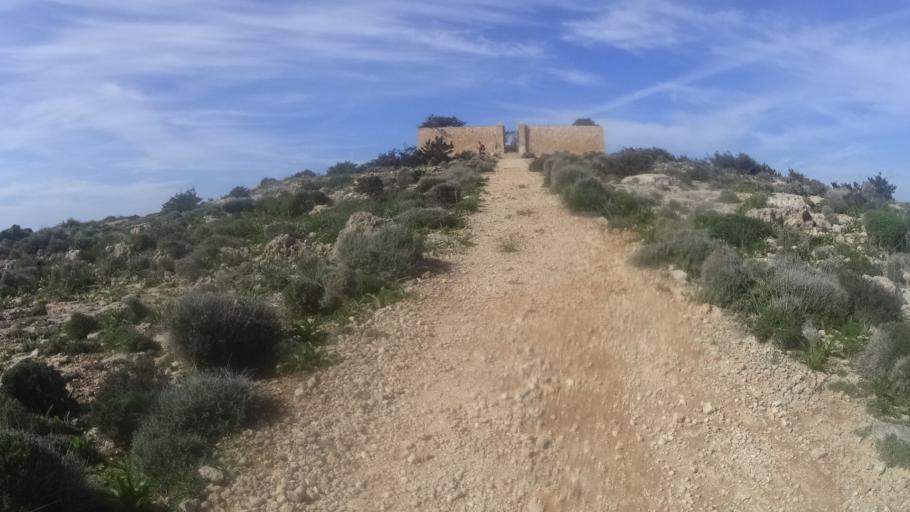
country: MT
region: Il-Qala
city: Qala
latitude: 36.0117
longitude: 14.3314
